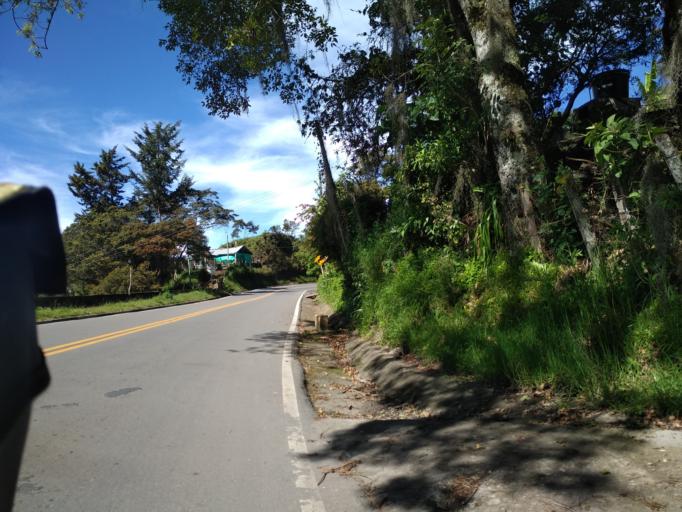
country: CO
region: Santander
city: Velez
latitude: 5.9997
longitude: -73.6839
